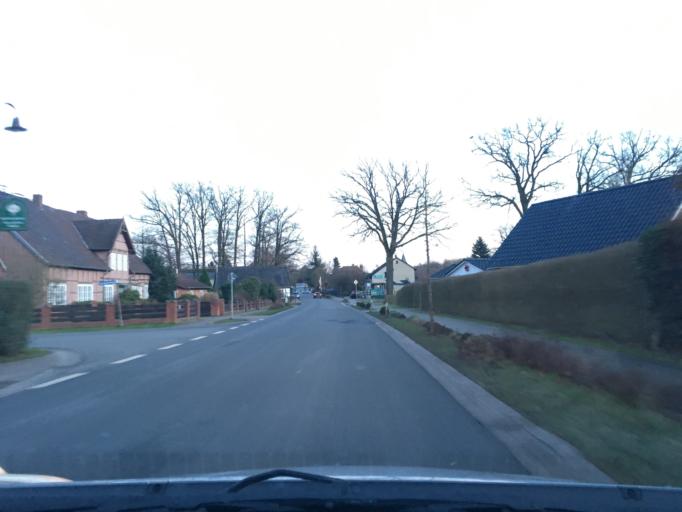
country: DE
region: Lower Saxony
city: Kusten
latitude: 52.9779
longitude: 11.0615
